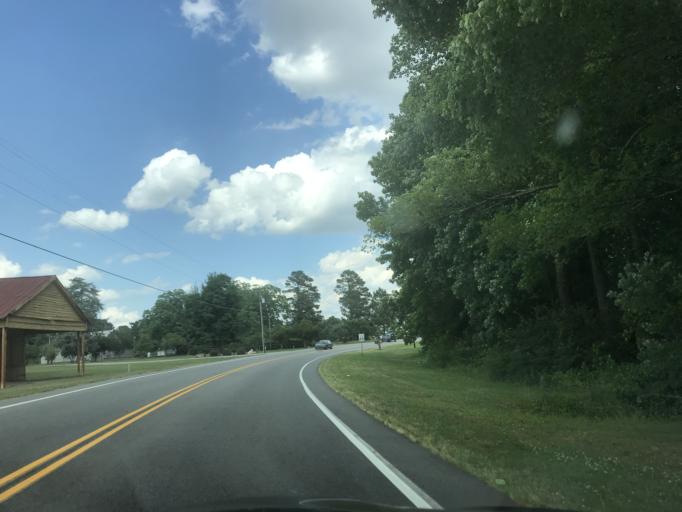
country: US
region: North Carolina
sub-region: Nash County
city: Spring Hope
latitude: 35.9622
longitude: -78.0601
